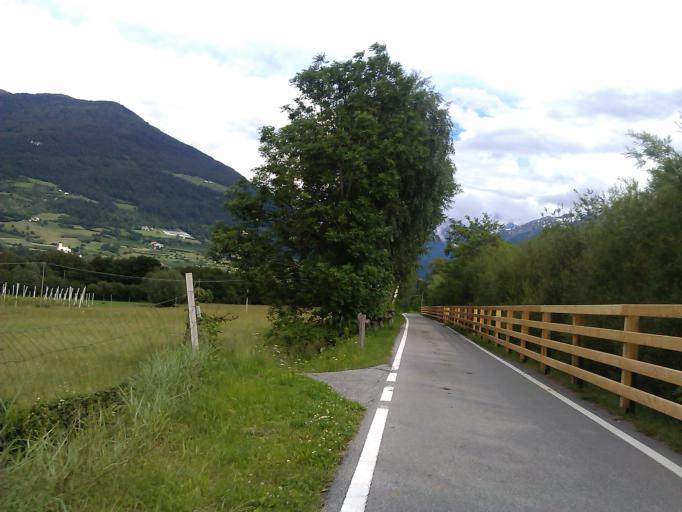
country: IT
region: Trentino-Alto Adige
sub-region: Bolzano
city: Glorenza
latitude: 46.6666
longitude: 10.5595
